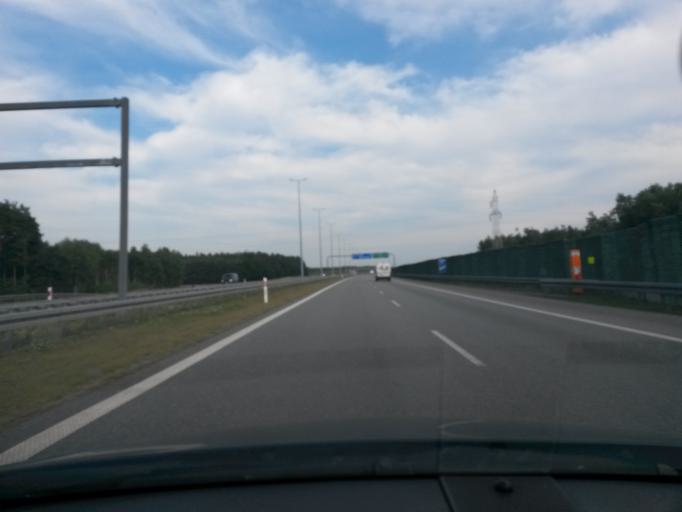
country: PL
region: Greater Poland Voivodeship
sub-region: Powiat koninski
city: Stare Miasto
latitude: 52.1583
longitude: 18.2563
